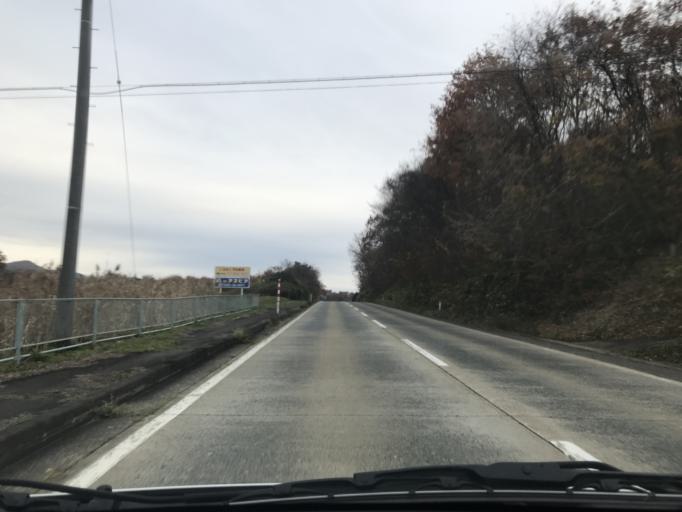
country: JP
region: Iwate
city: Kitakami
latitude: 39.2897
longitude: 141.2153
